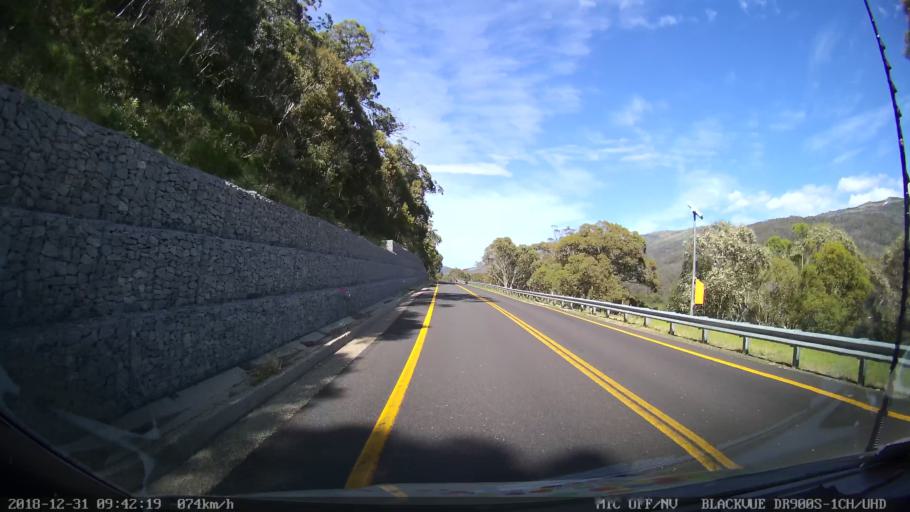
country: AU
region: New South Wales
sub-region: Snowy River
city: Jindabyne
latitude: -36.4958
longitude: 148.3243
